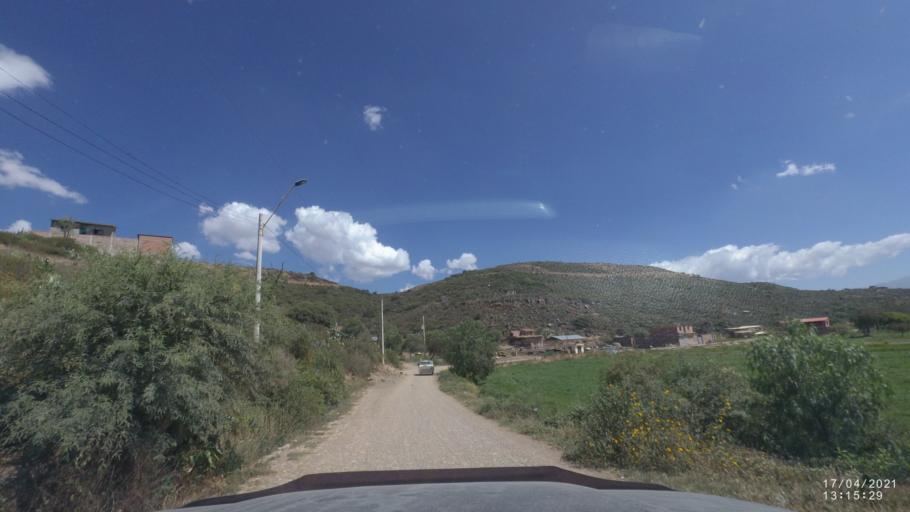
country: BO
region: Cochabamba
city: Cochabamba
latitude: -17.4174
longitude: -66.2315
